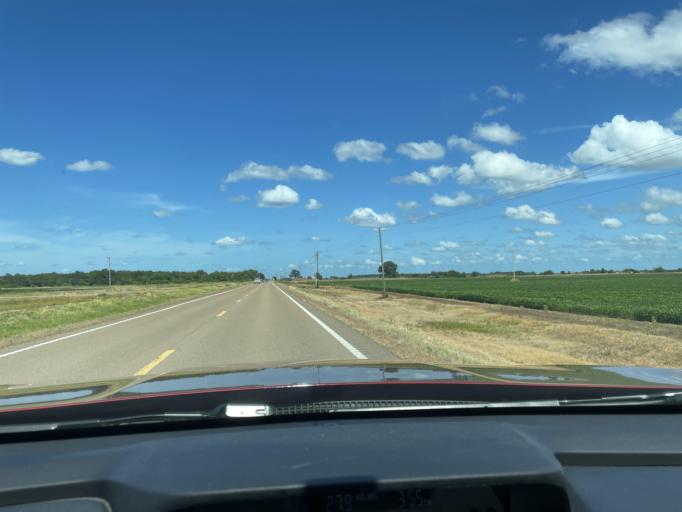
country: US
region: Mississippi
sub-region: Humphreys County
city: Belzoni
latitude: 33.1826
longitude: -90.6392
